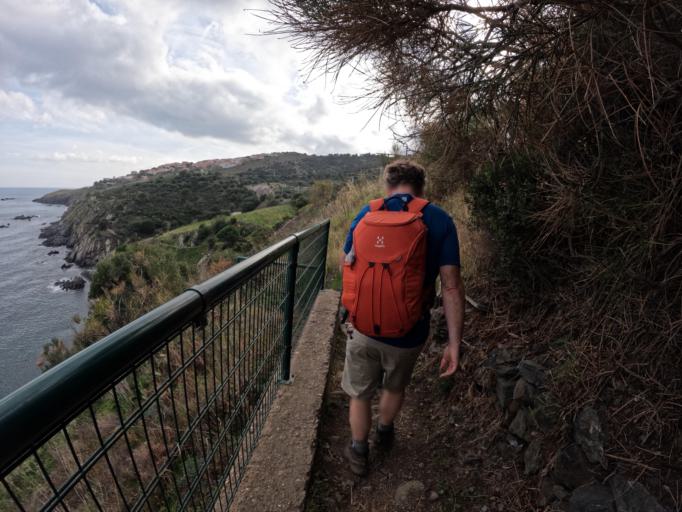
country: FR
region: Languedoc-Roussillon
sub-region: Departement des Pyrenees-Orientales
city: Cervera de la Marenda
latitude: 42.4526
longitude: 3.1593
